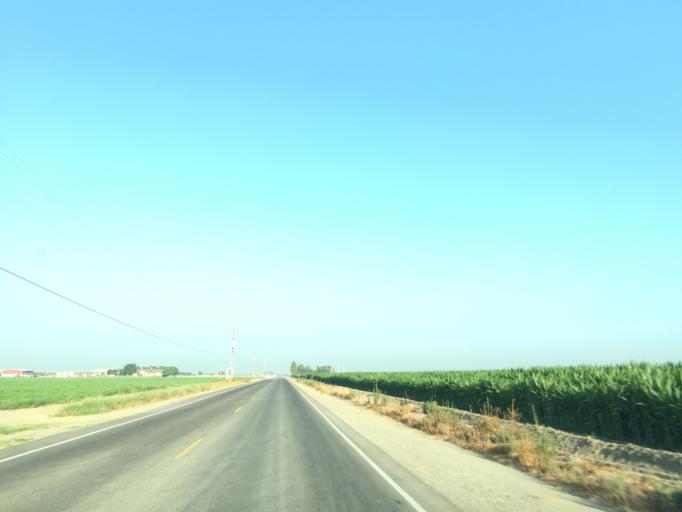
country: US
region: California
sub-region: Tulare County
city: London
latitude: 36.4582
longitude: -119.3720
